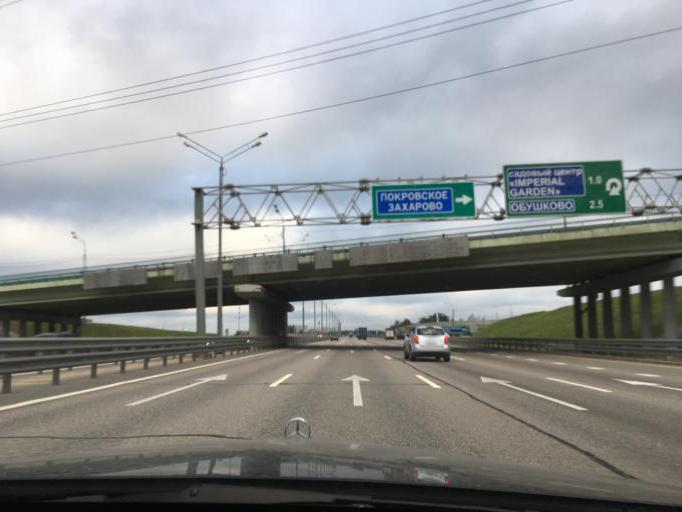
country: RU
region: Moskovskaya
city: Rozhdestveno
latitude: 55.8091
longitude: 37.0320
